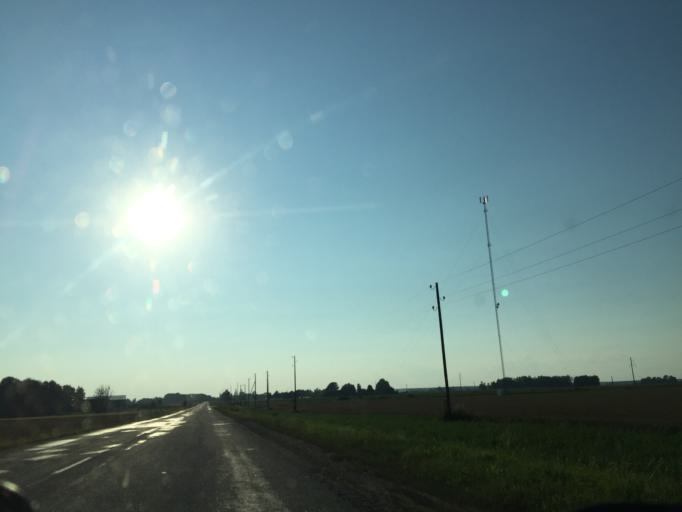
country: LV
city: Tervete
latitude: 56.4378
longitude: 23.5063
